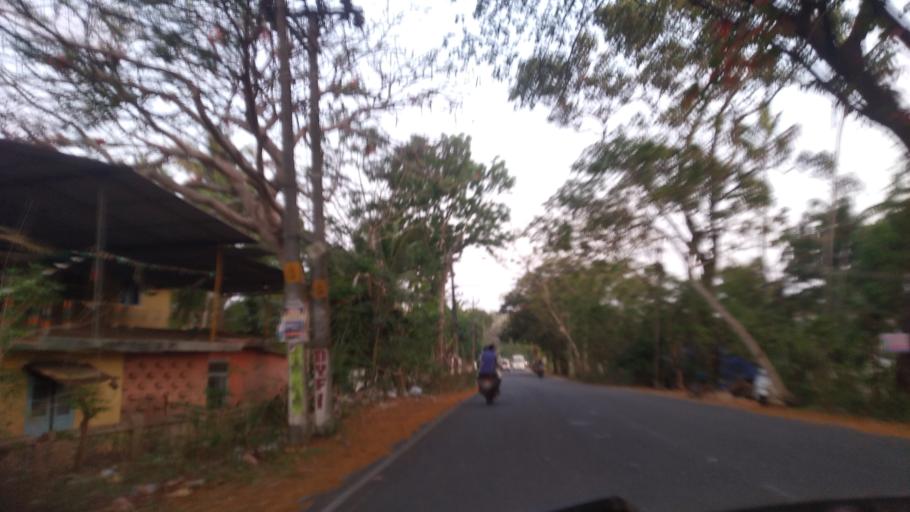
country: IN
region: Kerala
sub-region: Thrissur District
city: Kodungallur
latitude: 10.2073
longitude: 76.1642
